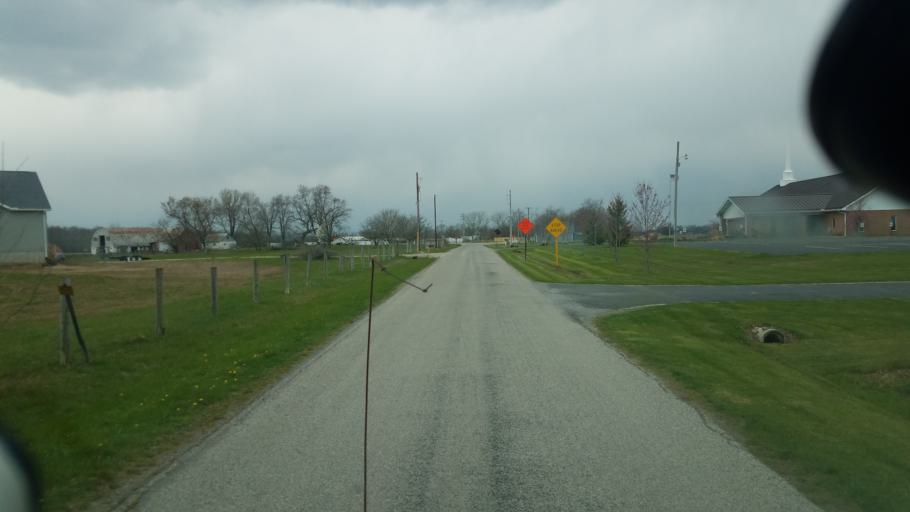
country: US
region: Ohio
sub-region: Union County
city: Richwood
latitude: 40.3947
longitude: -83.2670
